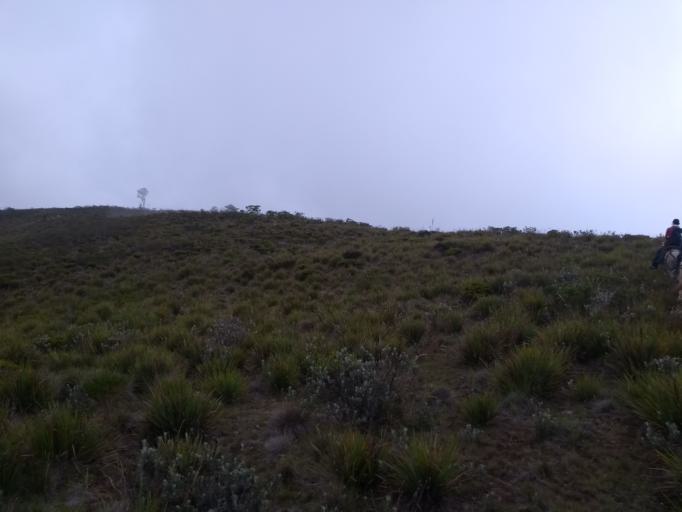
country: CO
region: Cesar
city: Manaure Balcon del Cesar
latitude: 10.2100
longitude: -73.0094
